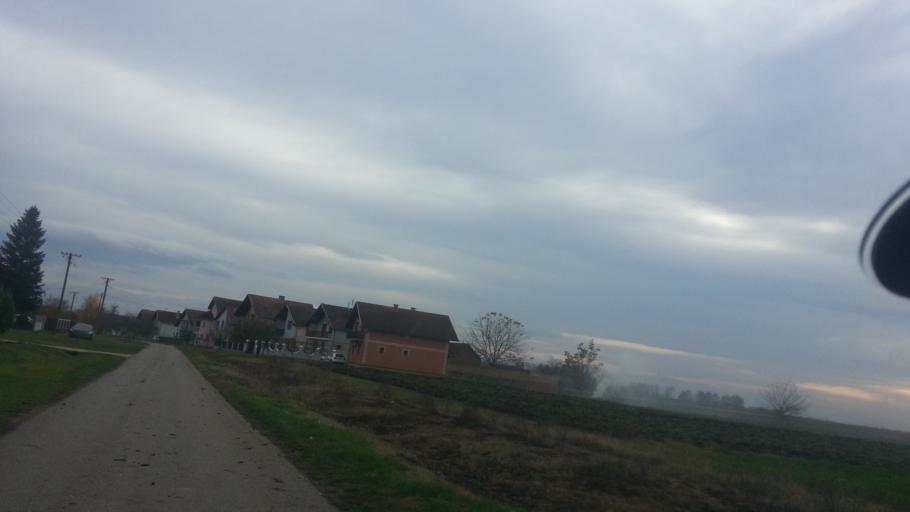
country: RS
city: Putinci
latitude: 44.9702
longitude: 19.9695
